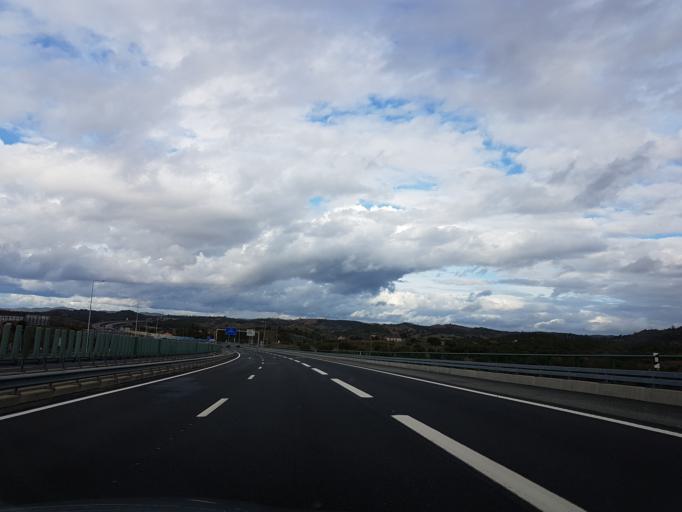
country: PT
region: Faro
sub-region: Silves
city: Sao Bartolomeu de Messines
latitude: 37.2505
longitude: -8.2551
